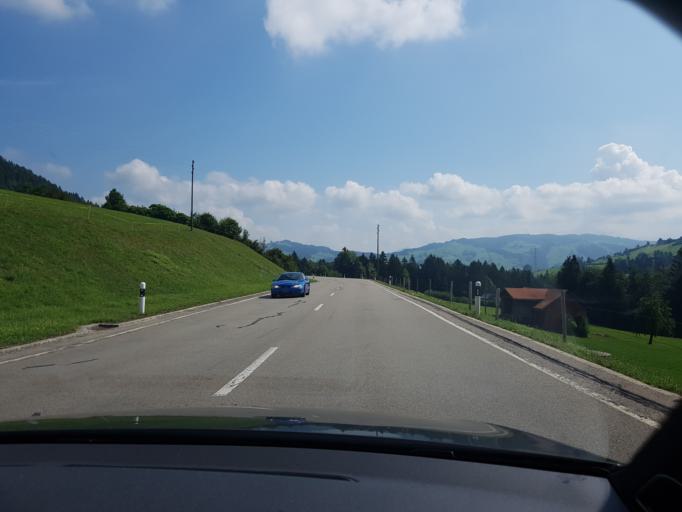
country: CH
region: Saint Gallen
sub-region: Wahlkreis Toggenburg
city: Wattwil
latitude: 47.2755
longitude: 9.0639
